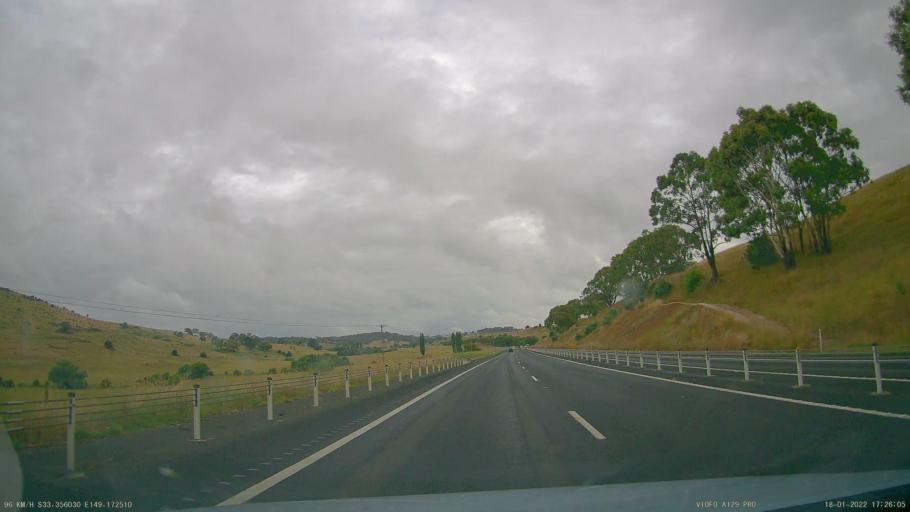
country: AU
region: New South Wales
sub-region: Blayney
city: Millthorpe
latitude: -33.3563
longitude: 149.1727
